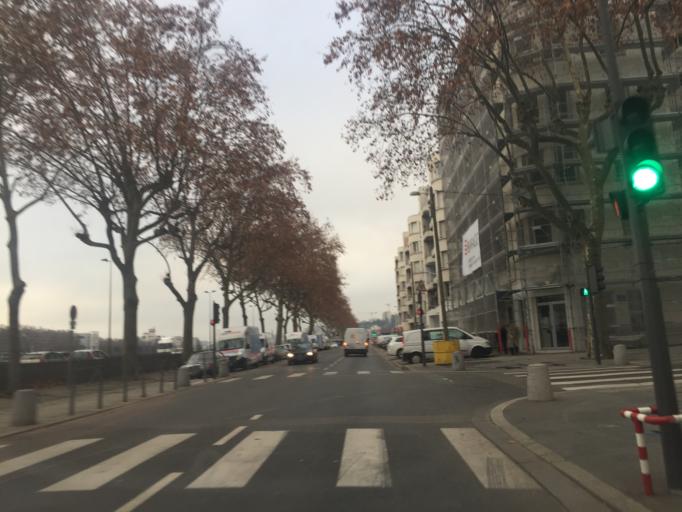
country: FR
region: Rhone-Alpes
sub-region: Departement du Rhone
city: Lyon
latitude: 45.7425
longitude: 4.8251
